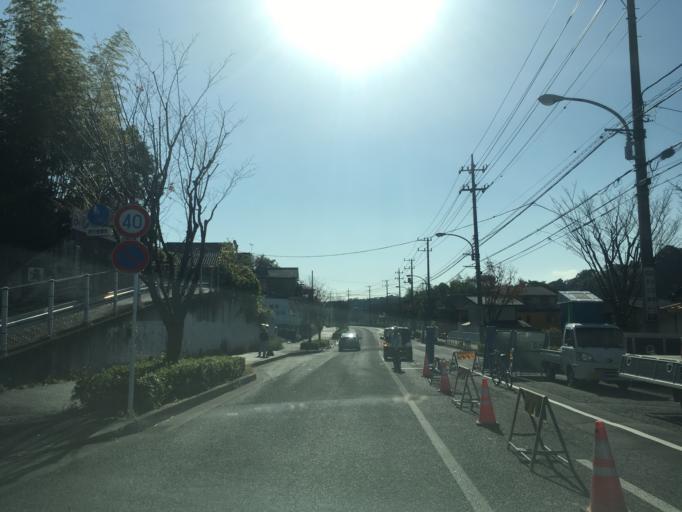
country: JP
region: Tokyo
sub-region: Machida-shi
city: Machida
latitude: 35.5898
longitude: 139.4185
